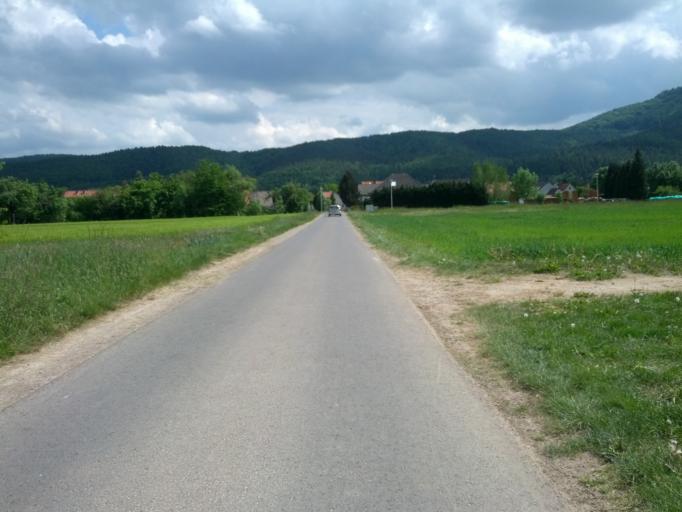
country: DE
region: Thuringia
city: Treffurt
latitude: 51.1311
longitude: 10.1979
